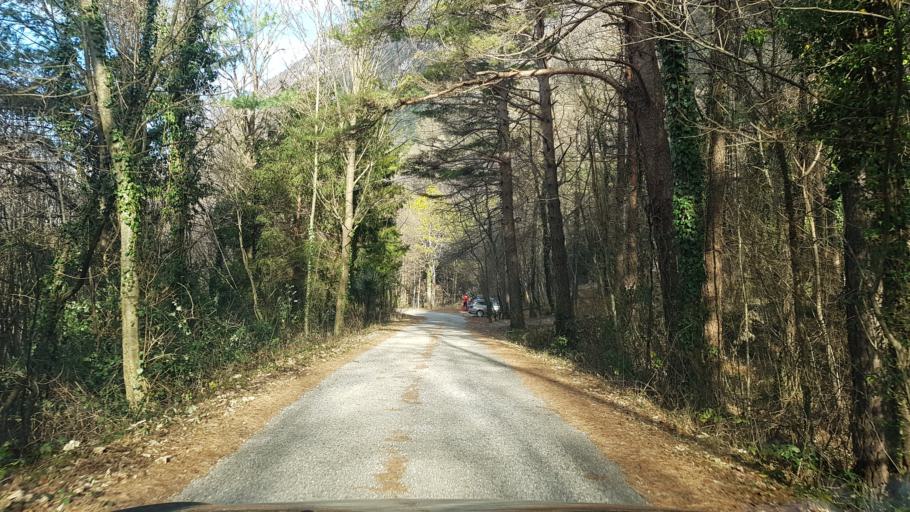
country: IT
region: Friuli Venezia Giulia
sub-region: Provincia di Udine
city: Gemona
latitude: 46.2844
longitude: 13.1532
